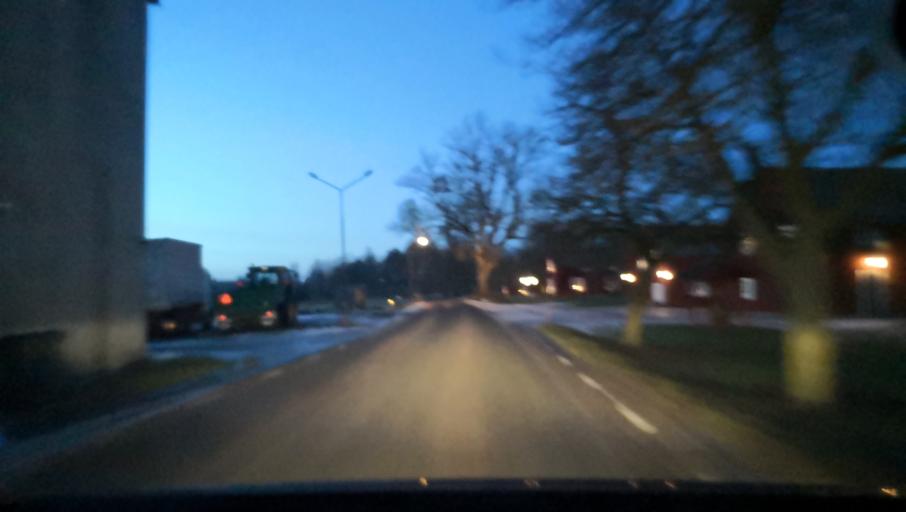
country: SE
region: Soedermanland
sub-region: Katrineholms Kommun
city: Katrineholm
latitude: 59.0695
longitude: 16.3562
